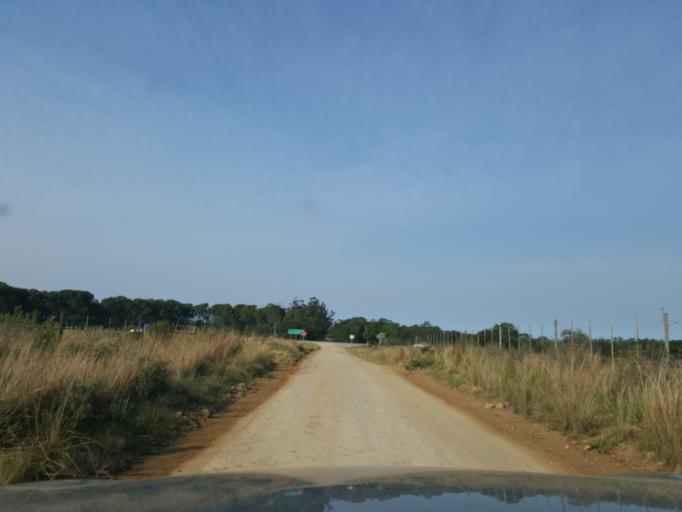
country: ZA
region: Eastern Cape
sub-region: Cacadu District Municipality
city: Grahamstown
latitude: -33.4299
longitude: 26.3214
